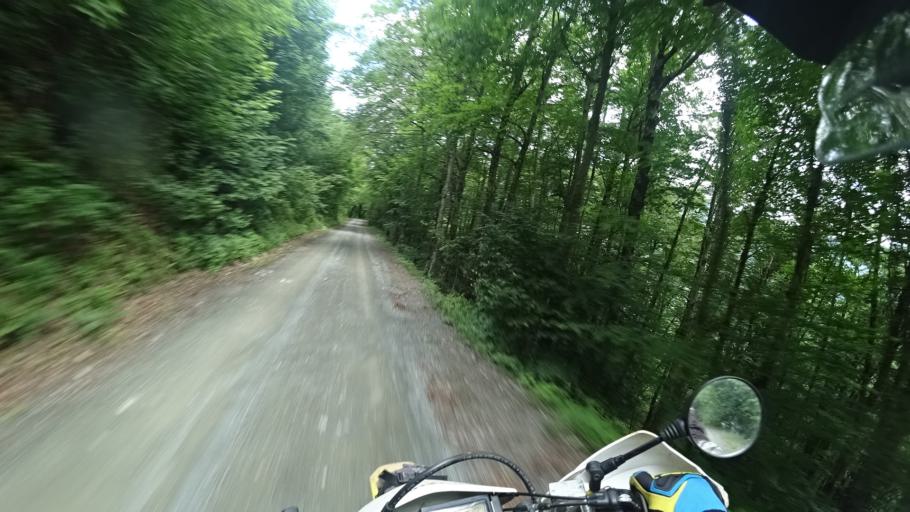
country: SI
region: Osilnica
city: Osilnica
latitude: 45.5202
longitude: 14.7203
